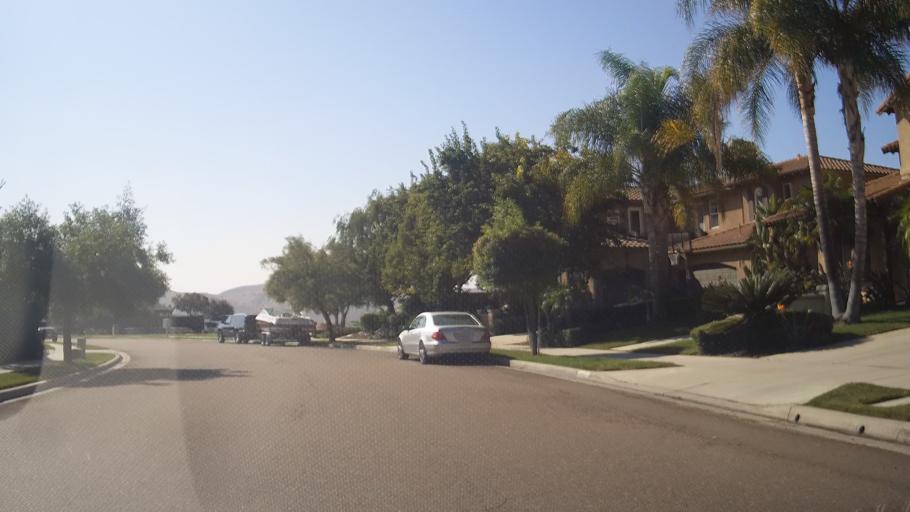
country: US
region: California
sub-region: San Diego County
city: Fairbanks Ranch
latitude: 33.0092
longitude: -117.1213
